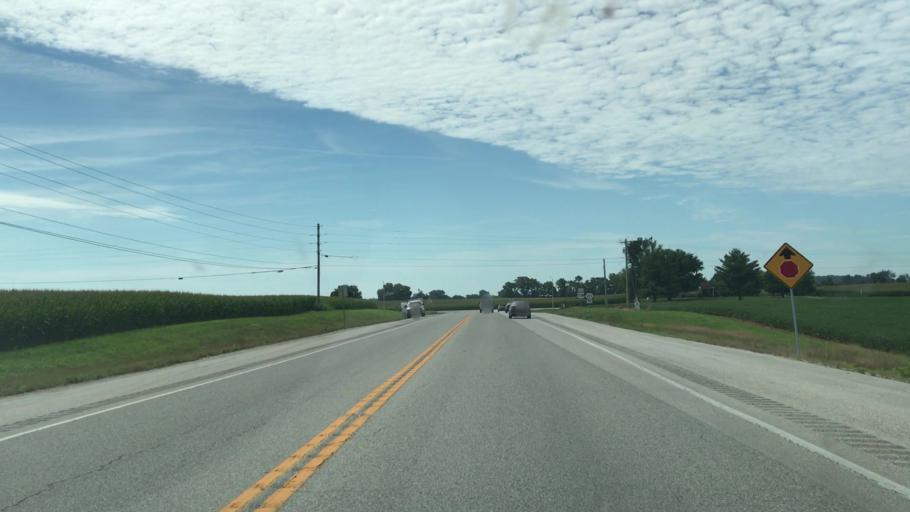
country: US
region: Kentucky
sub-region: Edmonson County
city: Brownsville
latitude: 37.0874
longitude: -86.2297
